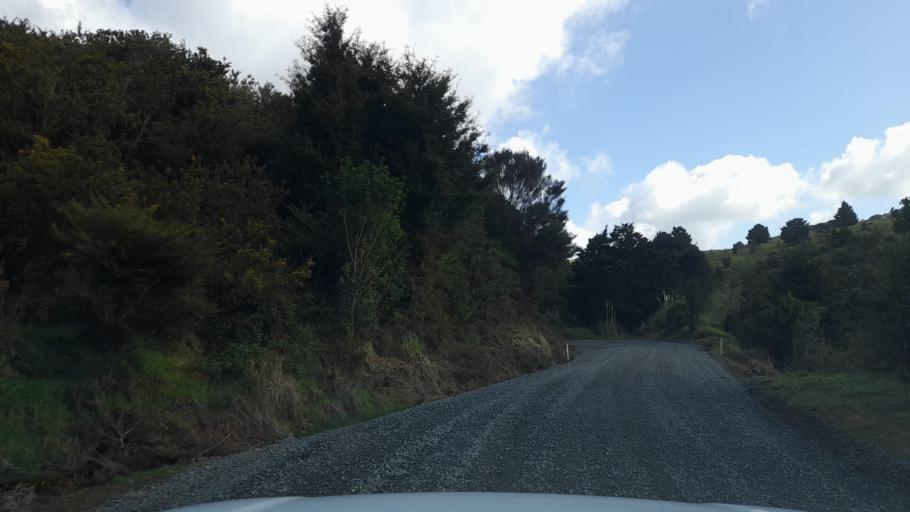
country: NZ
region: Northland
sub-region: Far North District
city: Kerikeri
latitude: -35.1325
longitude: 173.7346
